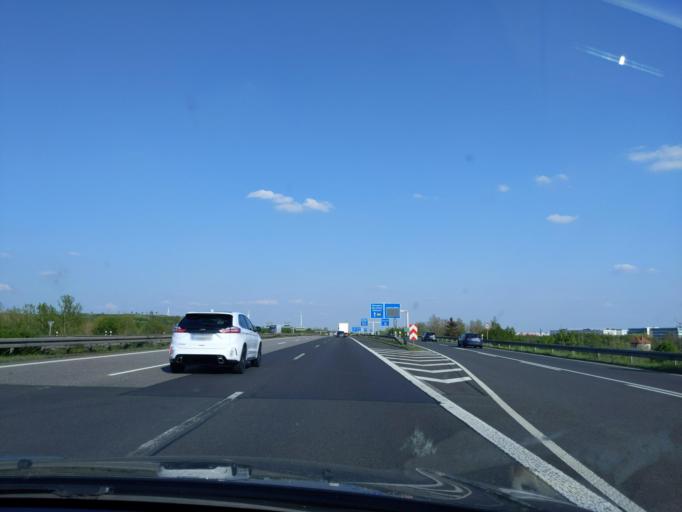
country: DE
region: Saxony
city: Rackwitz
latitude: 51.4080
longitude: 12.3801
